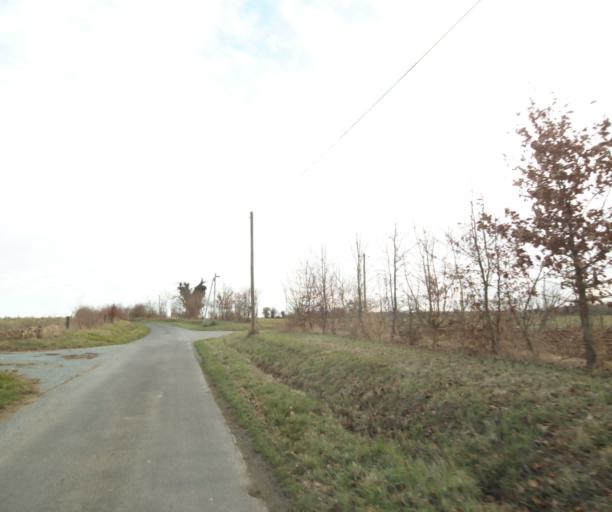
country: FR
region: Poitou-Charentes
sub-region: Departement de la Charente-Maritime
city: Corme-Royal
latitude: 45.7784
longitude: -0.8116
